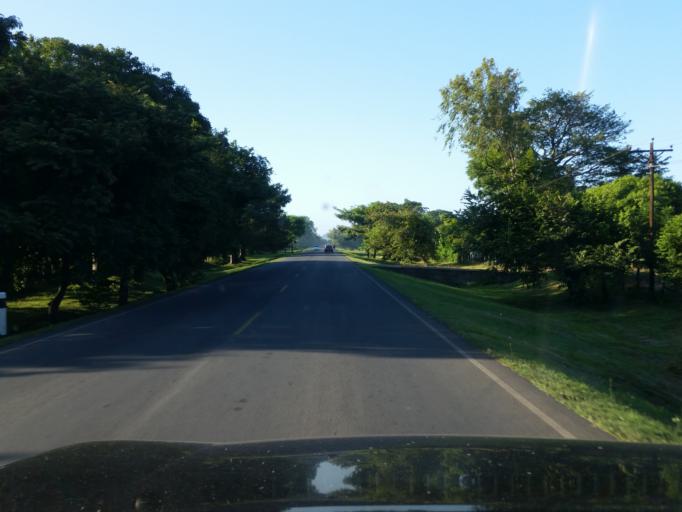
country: NI
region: Rivas
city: Potosi
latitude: 11.4857
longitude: -85.8698
